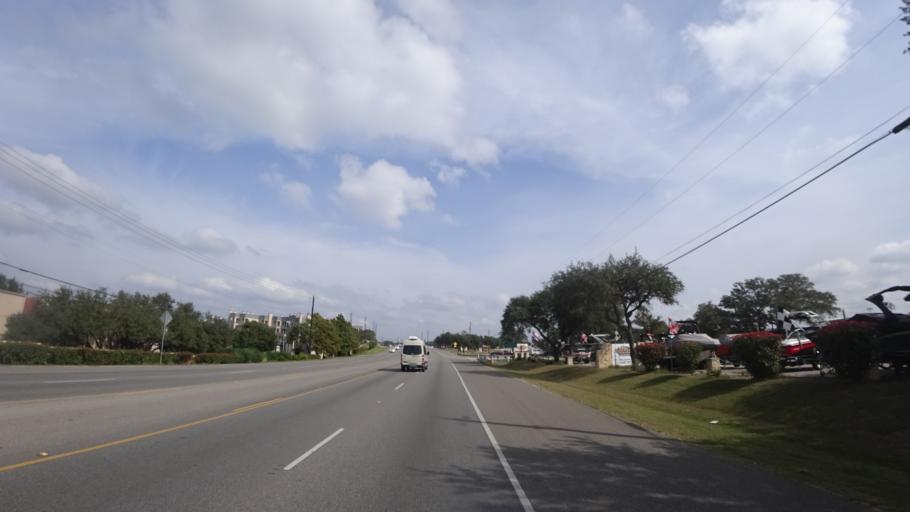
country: US
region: Texas
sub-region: Travis County
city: Hudson Bend
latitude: 30.3912
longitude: -97.9380
